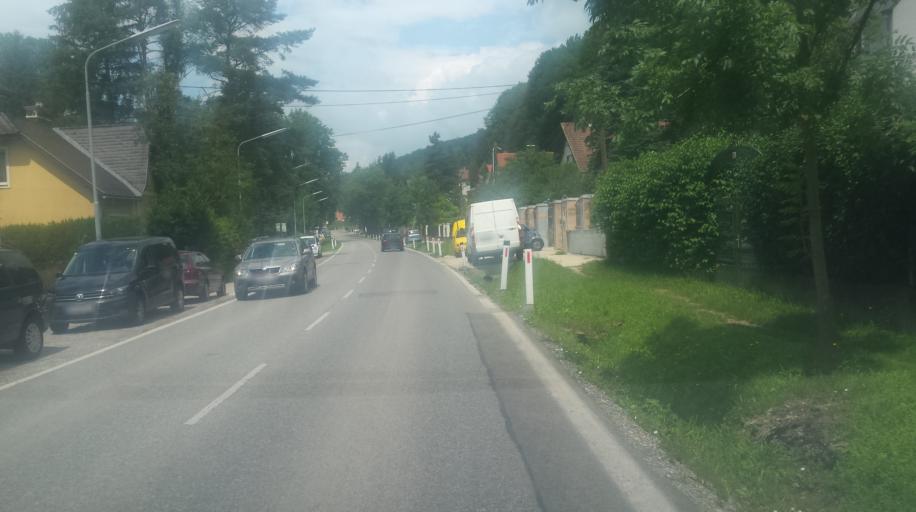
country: AT
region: Lower Austria
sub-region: Politischer Bezirk Wien-Umgebung
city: Purkersdorf
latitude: 48.2257
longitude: 16.2083
